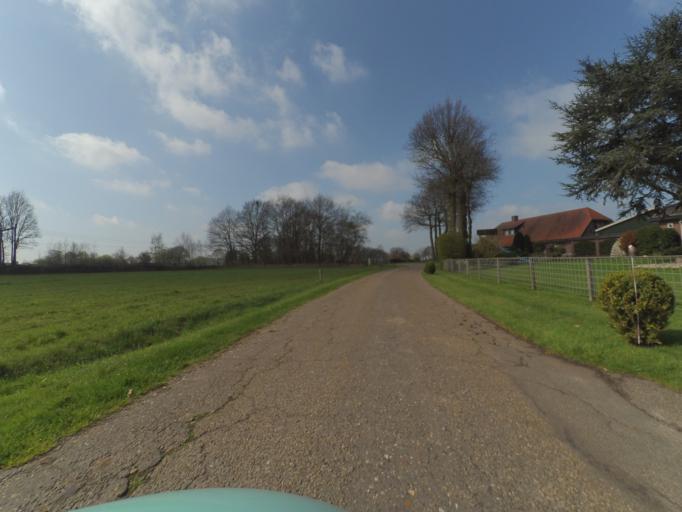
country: NL
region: Gelderland
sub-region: Gemeente Barneveld
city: Barneveld
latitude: 52.1632
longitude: 5.5577
